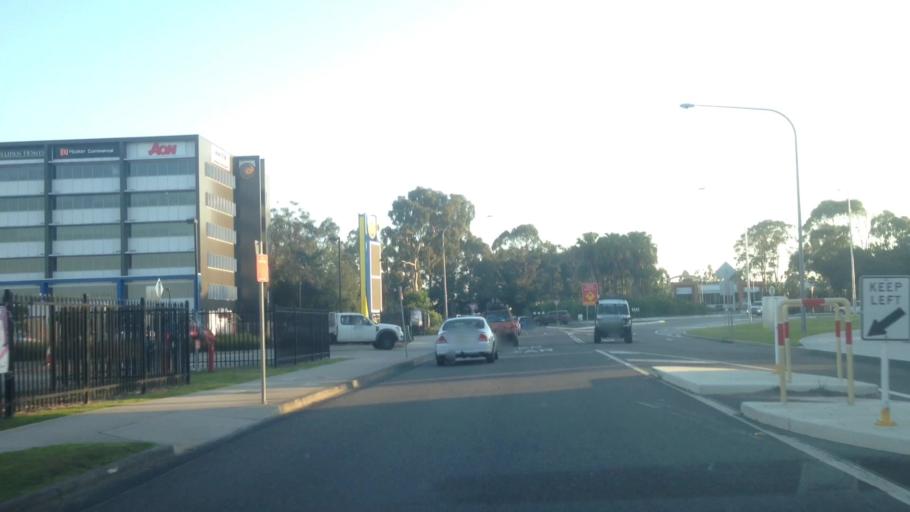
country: AU
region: New South Wales
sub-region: Wyong Shire
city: Chittaway Bay
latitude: -33.3119
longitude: 151.4223
